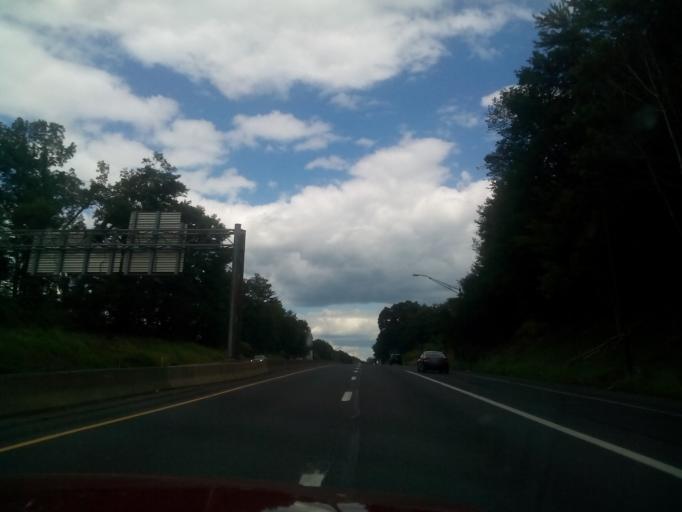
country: US
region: Pennsylvania
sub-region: Monroe County
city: East Stroudsburg
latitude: 40.9916
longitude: -75.1717
